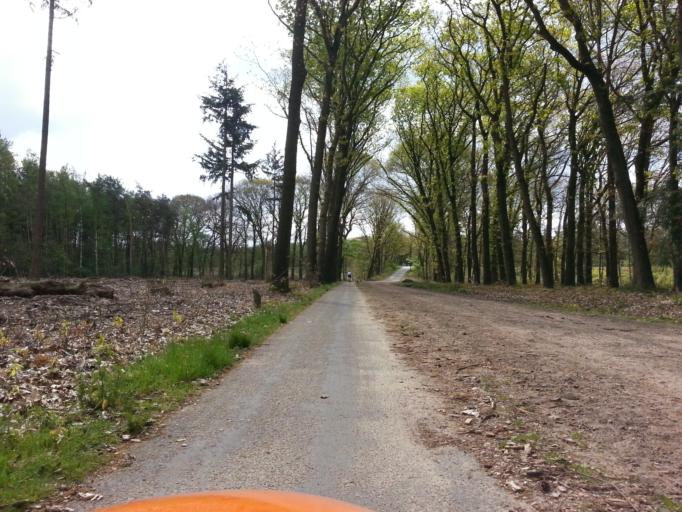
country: NL
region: Gelderland
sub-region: Gemeente Renkum
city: Heelsum
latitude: 52.0148
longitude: 5.7513
